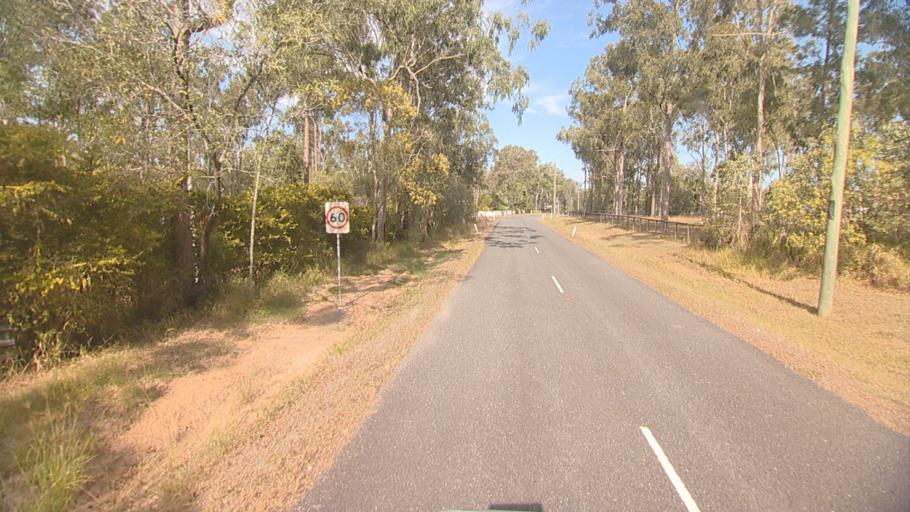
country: AU
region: Queensland
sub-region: Logan
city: North Maclean
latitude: -27.7461
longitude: 152.9736
